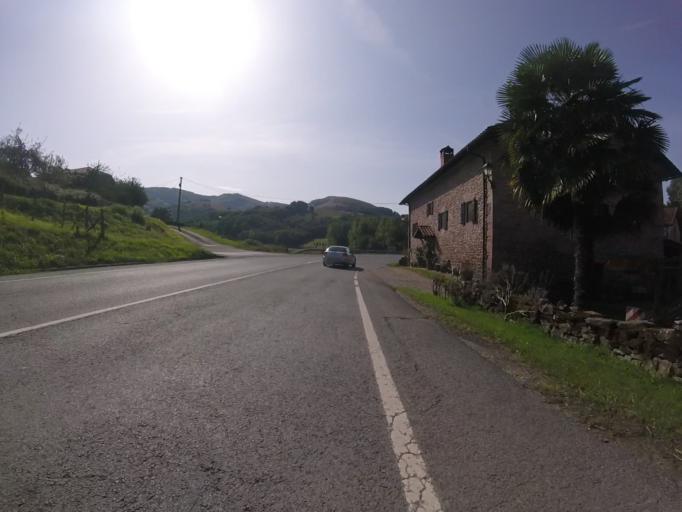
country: ES
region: Navarre
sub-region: Provincia de Navarra
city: Zugarramurdi
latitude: 43.1621
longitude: -1.4958
